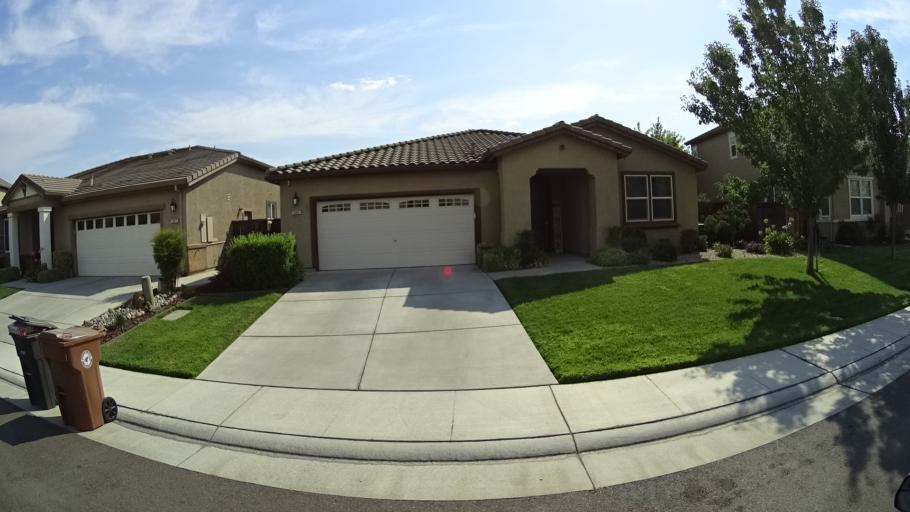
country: US
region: California
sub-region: Sacramento County
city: Laguna
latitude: 38.3767
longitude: -121.4465
